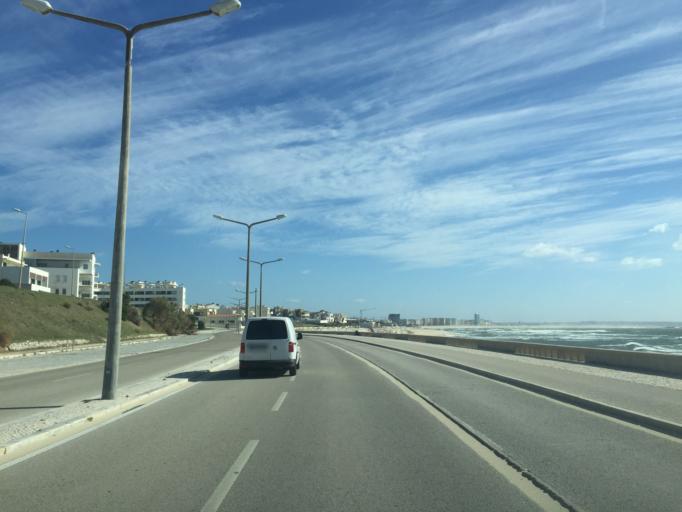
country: PT
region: Coimbra
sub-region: Figueira da Foz
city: Buarcos
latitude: 40.1716
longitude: -8.8924
